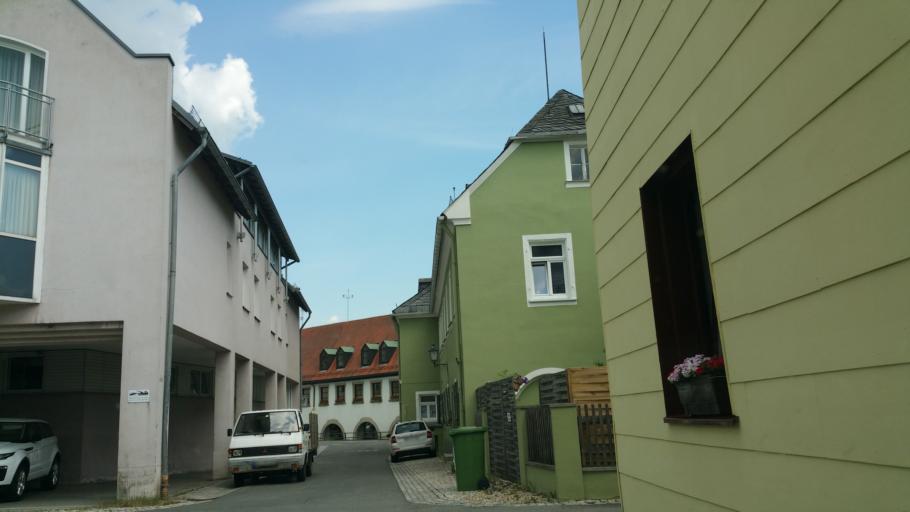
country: DE
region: Bavaria
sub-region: Upper Franconia
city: Schwarzenbach an der Saale
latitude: 50.2220
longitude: 11.9318
